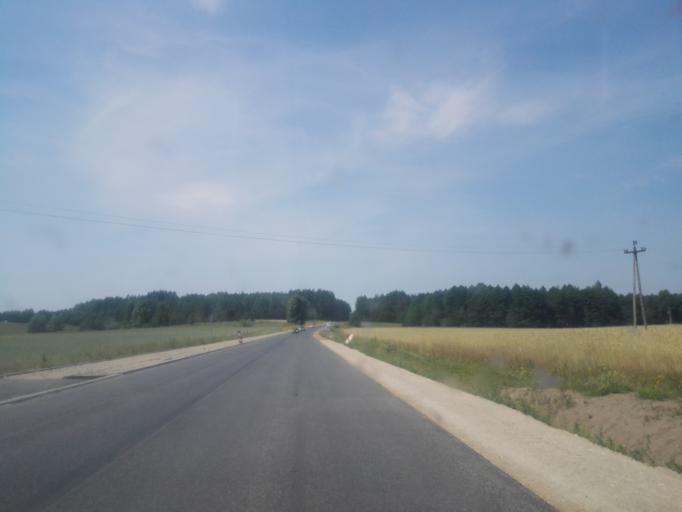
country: PL
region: Podlasie
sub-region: Powiat sejnenski
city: Krasnopol
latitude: 54.0820
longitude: 23.1097
